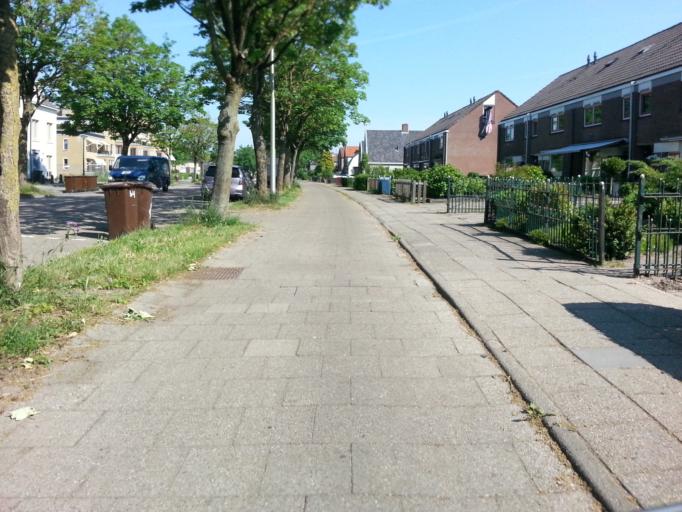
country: NL
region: Utrecht
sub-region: Gemeente Wijk bij Duurstede
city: Wijk bij Duurstede
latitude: 51.9766
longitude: 5.3449
